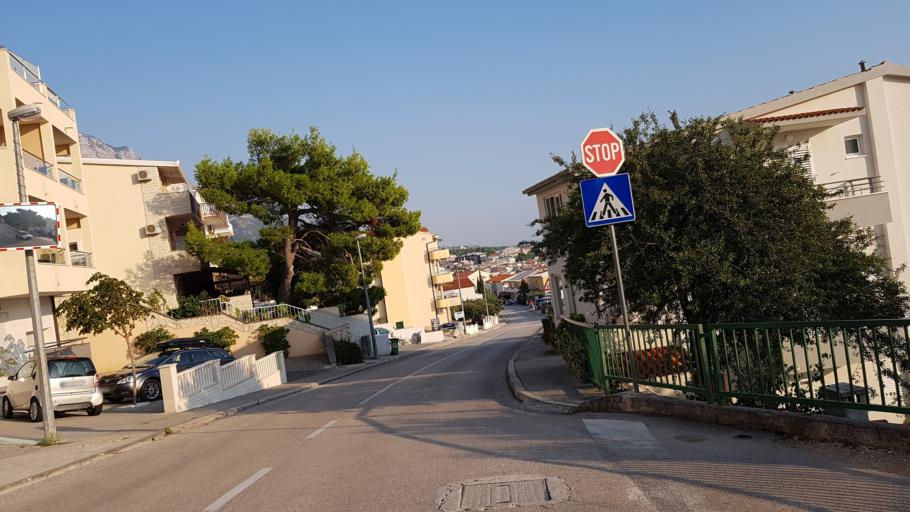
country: HR
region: Splitsko-Dalmatinska
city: Baska Voda
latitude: 43.3620
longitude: 16.9452
